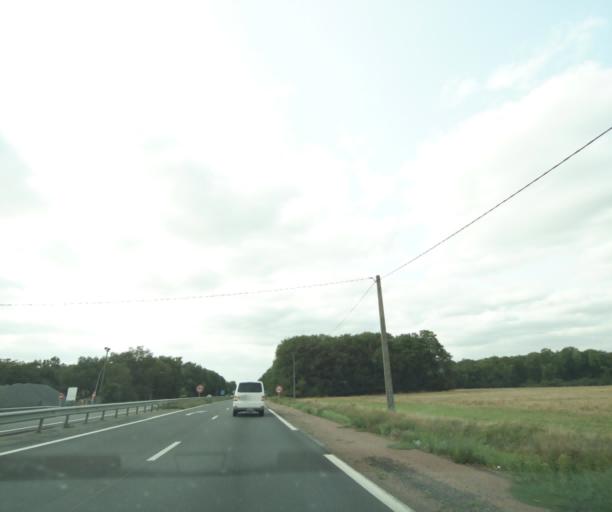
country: FR
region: Centre
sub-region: Departement d'Indre-et-Loire
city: Esvres
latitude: 47.3034
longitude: 0.7936
